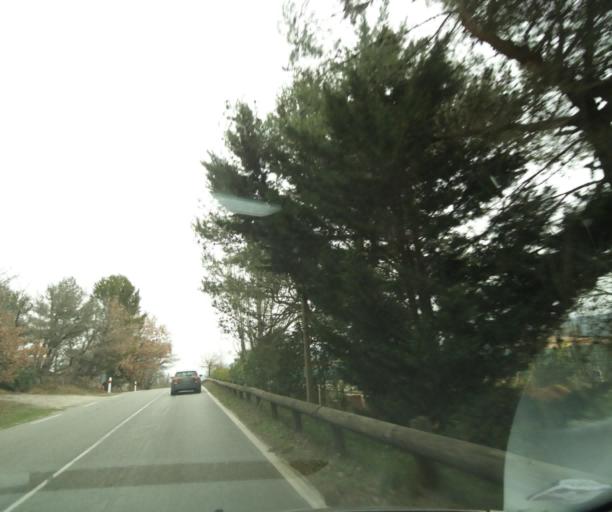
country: FR
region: Provence-Alpes-Cote d'Azur
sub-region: Departement des Bouches-du-Rhone
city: Trets
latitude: 43.4487
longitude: 5.6642
